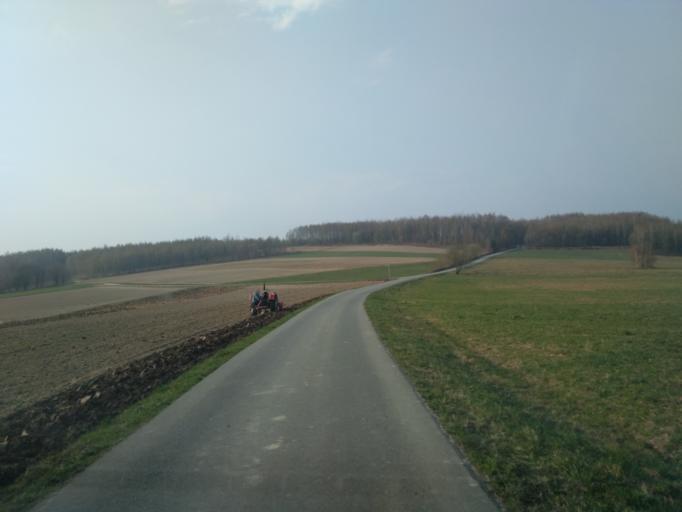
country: PL
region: Subcarpathian Voivodeship
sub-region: Powiat ropczycko-sedziszowski
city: Wielopole Skrzynskie
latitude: 49.9063
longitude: 21.5935
